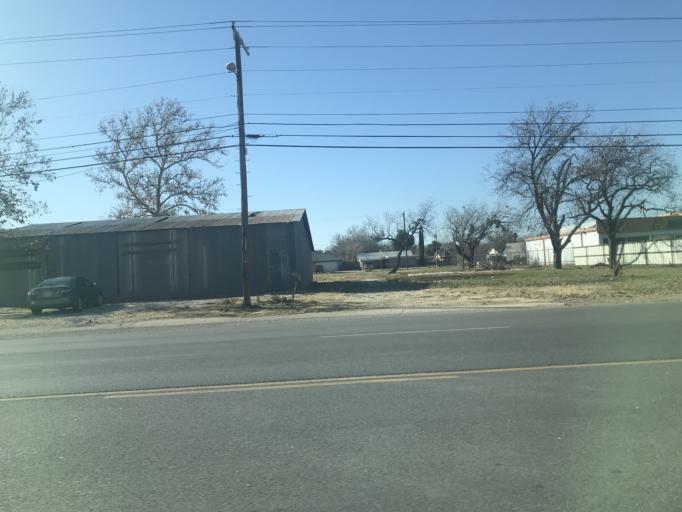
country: US
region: Texas
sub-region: Taylor County
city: Abilene
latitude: 32.4129
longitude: -99.7424
